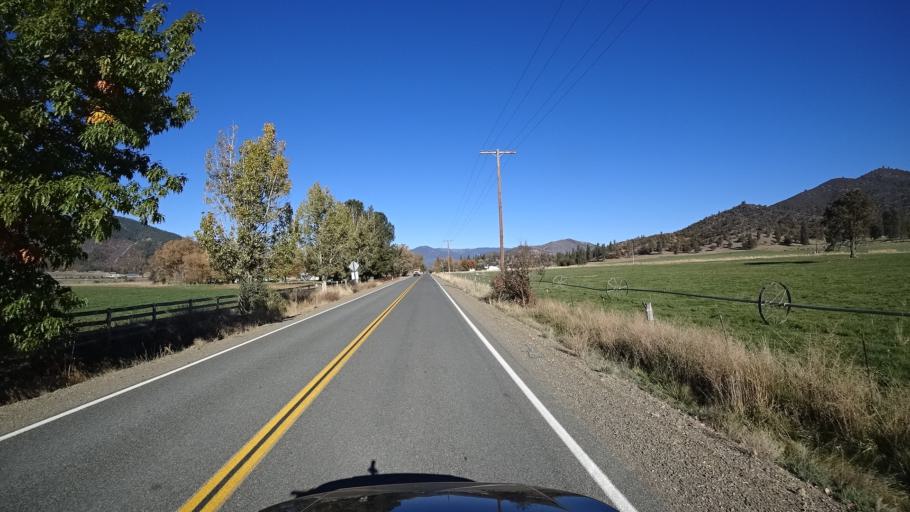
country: US
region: California
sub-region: Siskiyou County
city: Yreka
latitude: 41.5900
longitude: -122.8372
